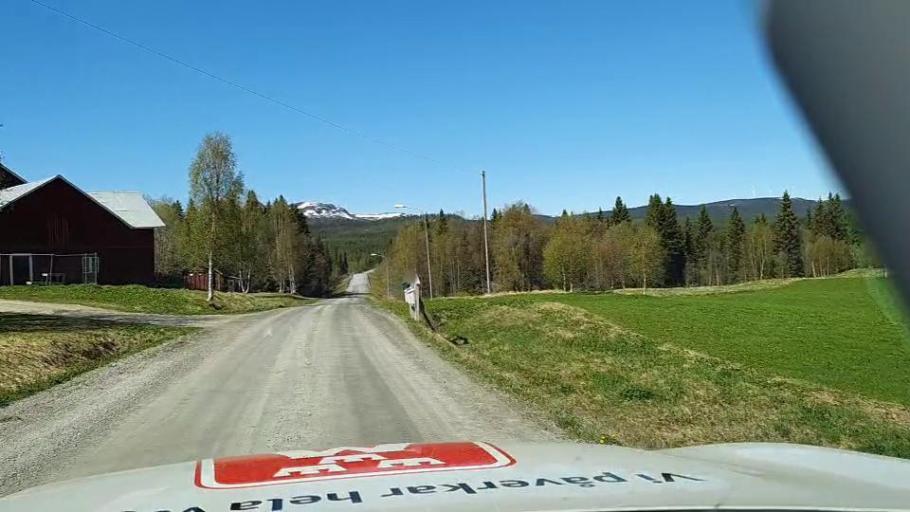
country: SE
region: Jaemtland
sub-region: Krokoms Kommun
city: Valla
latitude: 63.7003
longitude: 13.6011
